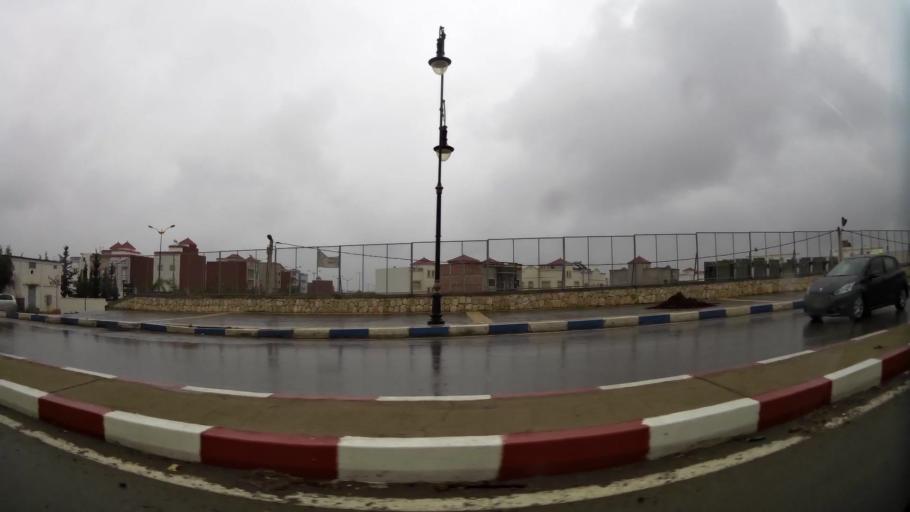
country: MA
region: Taza-Al Hoceima-Taounate
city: Imzourene
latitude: 35.1496
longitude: -3.8450
